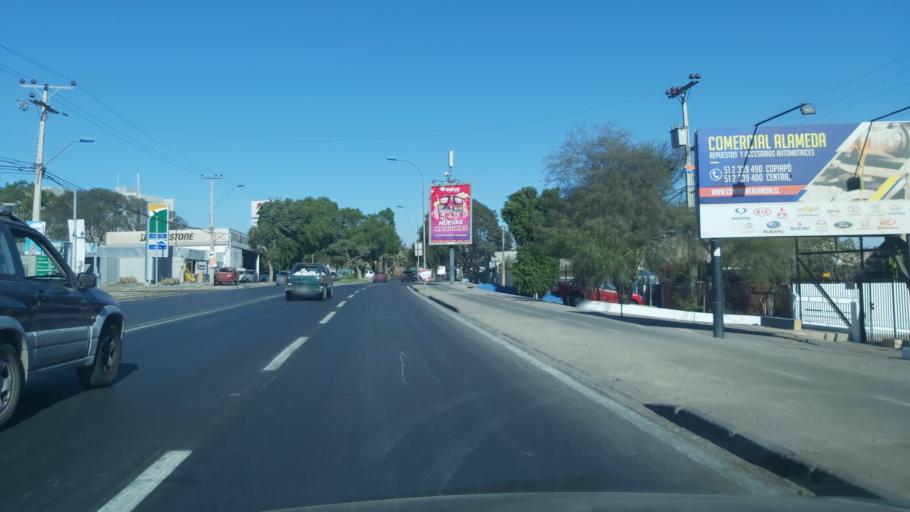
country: CL
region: Atacama
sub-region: Provincia de Copiapo
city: Copiapo
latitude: -27.3719
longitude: -70.3320
